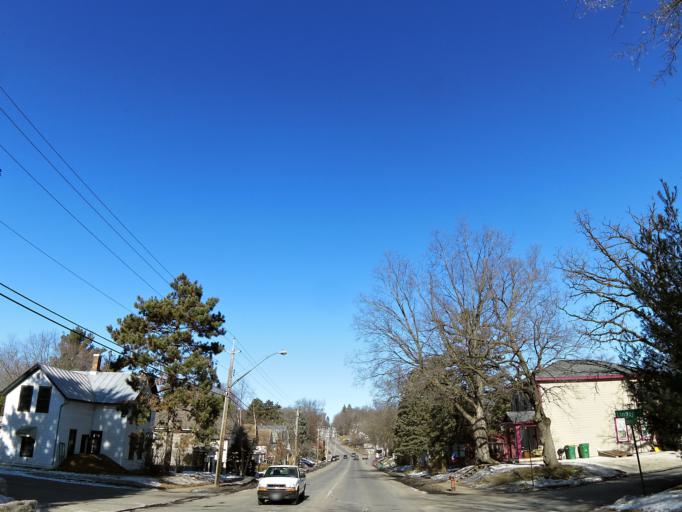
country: US
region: Minnesota
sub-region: Washington County
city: Stillwater
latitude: 45.0580
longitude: -92.8204
